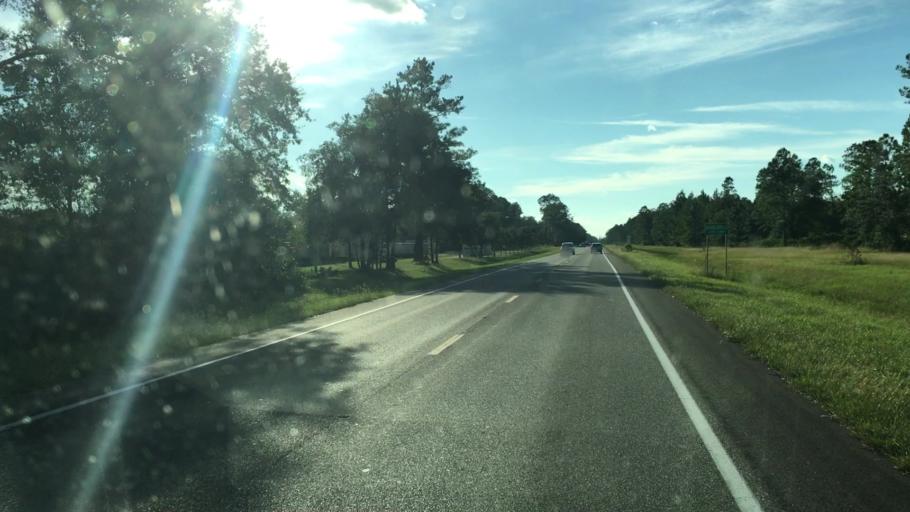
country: US
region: Florida
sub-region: Alachua County
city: Gainesville
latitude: 29.7030
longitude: -82.2845
